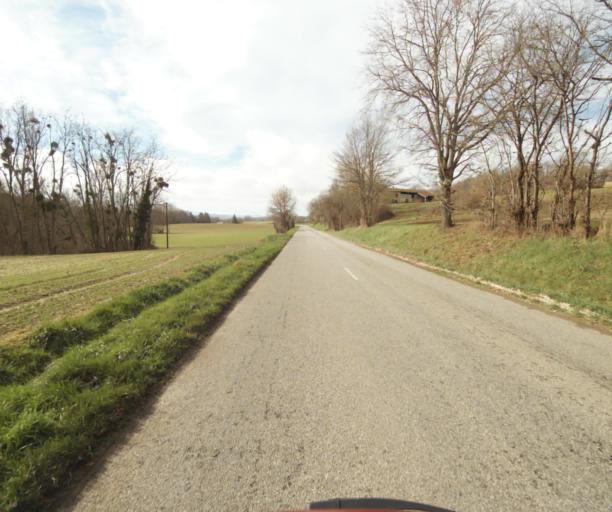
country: FR
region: Midi-Pyrenees
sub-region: Departement de l'Ariege
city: Pamiers
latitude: 43.1404
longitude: 1.5660
